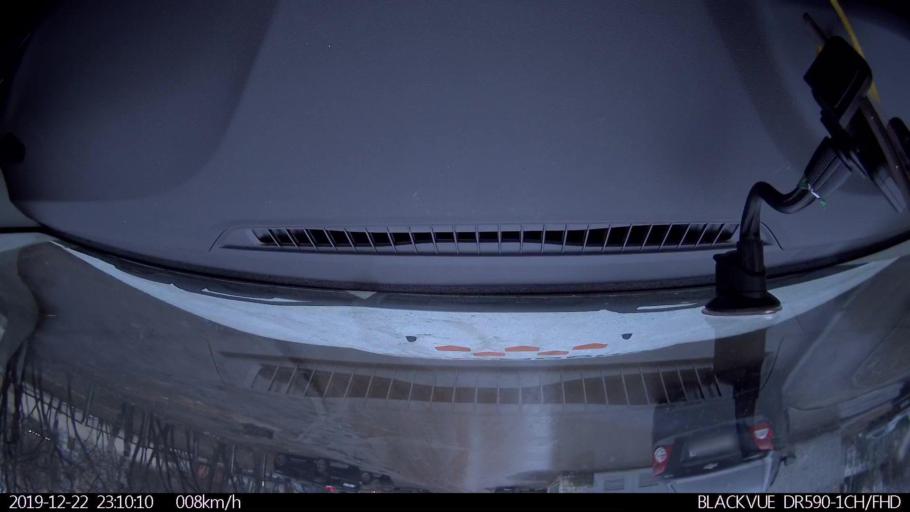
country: RU
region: Nizjnij Novgorod
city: Gorbatovka
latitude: 56.2609
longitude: 43.8507
